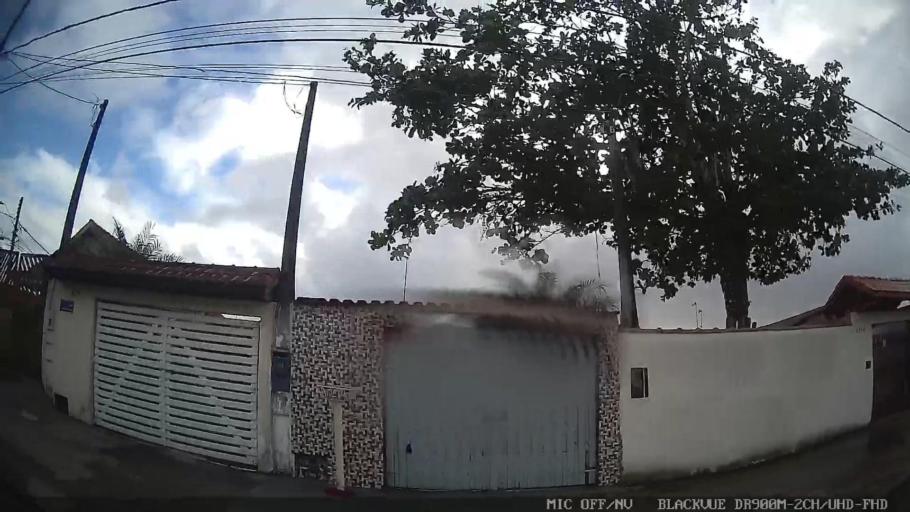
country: BR
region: Sao Paulo
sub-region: Itanhaem
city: Itanhaem
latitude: -24.2385
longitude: -46.9014
